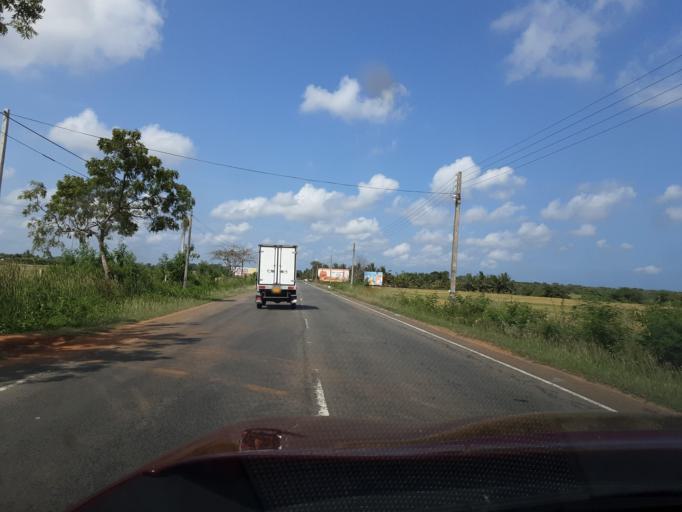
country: LK
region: Southern
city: Tangalla
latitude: 6.2175
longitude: 81.2122
